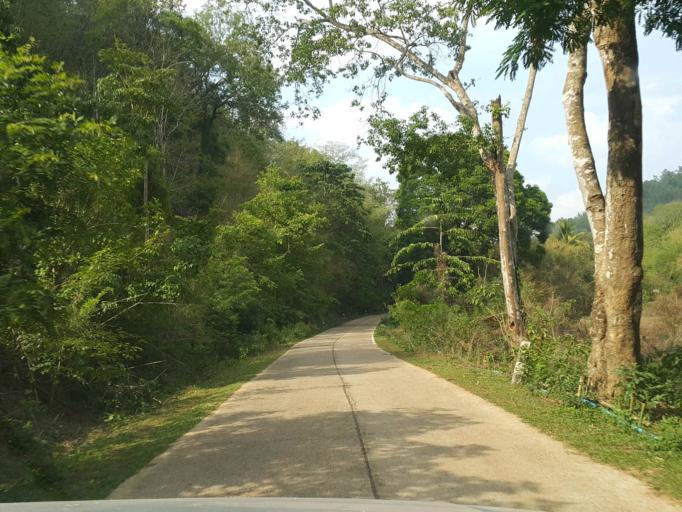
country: TH
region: Chiang Mai
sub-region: Amphoe Chiang Dao
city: Chiang Dao
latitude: 19.4030
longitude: 98.7828
